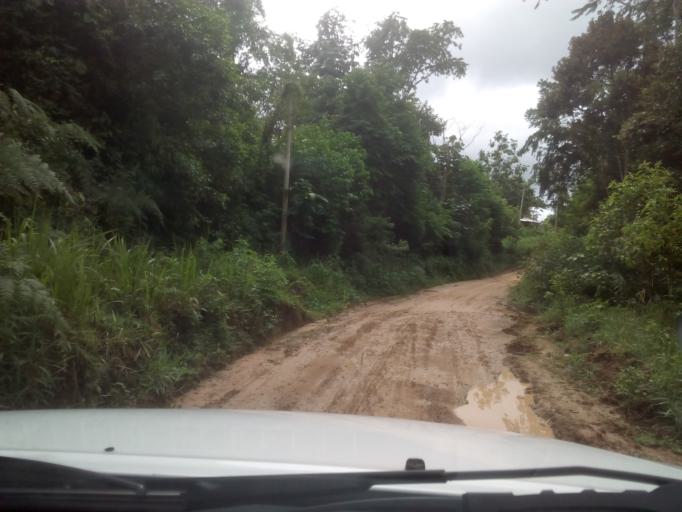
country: PE
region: San Martin
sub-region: Provincia de Lamas
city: Lamas
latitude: -6.4166
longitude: -76.4599
